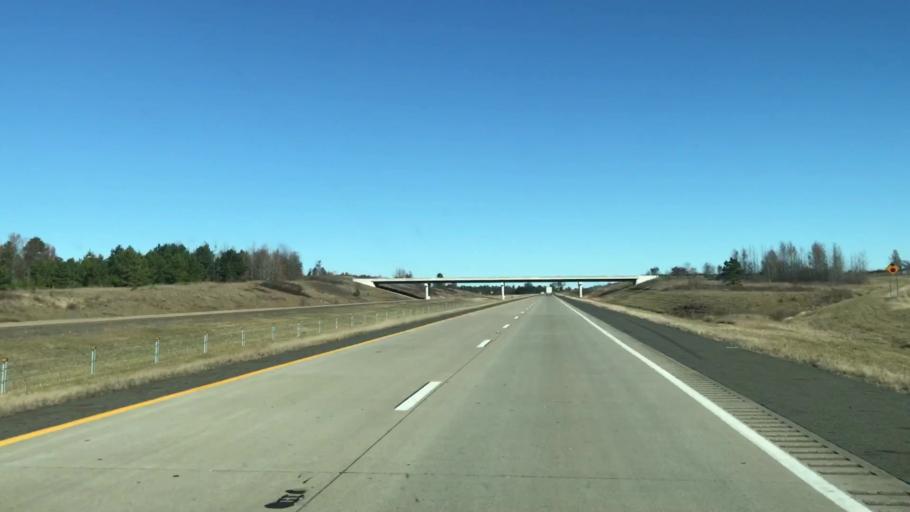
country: US
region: Texas
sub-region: Cass County
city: Queen City
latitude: 33.1173
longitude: -93.8936
